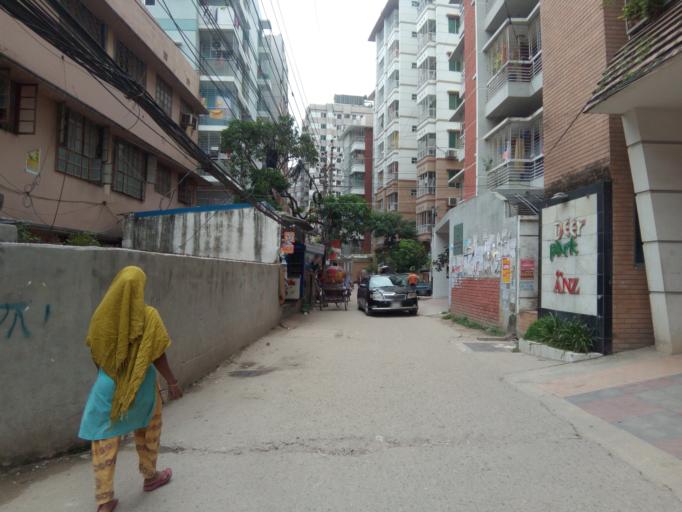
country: BD
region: Dhaka
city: Paltan
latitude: 23.7490
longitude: 90.4101
